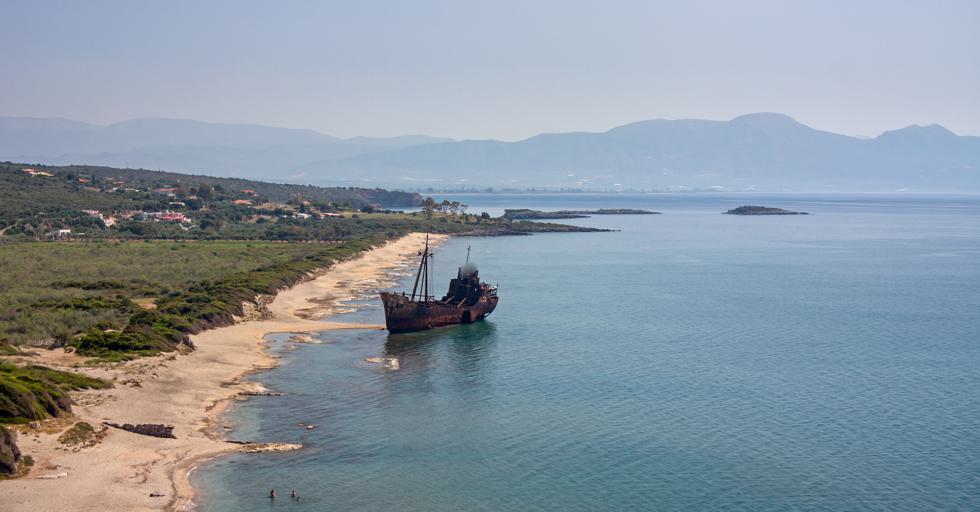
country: GR
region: Peloponnese
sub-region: Nomos Lakonias
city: Gytheio
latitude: 36.7877
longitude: 22.5807
